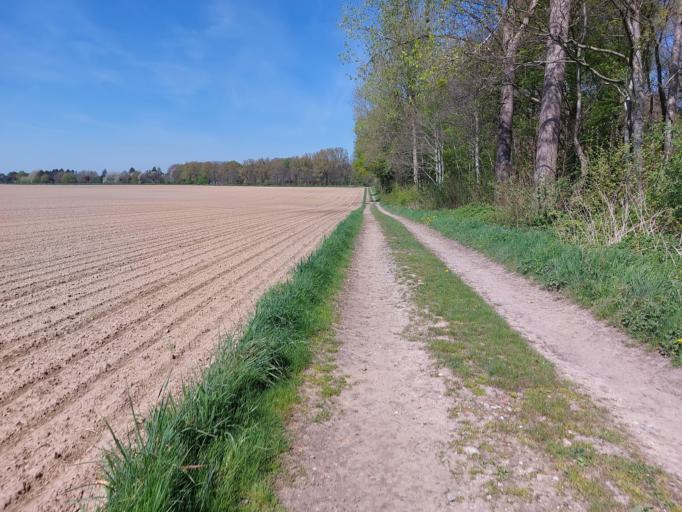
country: BE
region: Wallonia
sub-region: Province du Hainaut
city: Silly
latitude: 50.6150
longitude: 3.9693
